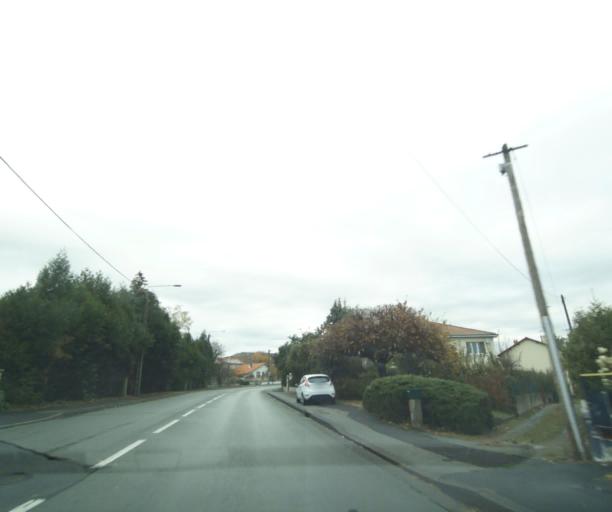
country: FR
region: Auvergne
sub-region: Departement du Puy-de-Dome
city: Cournon-d'Auvergne
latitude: 45.7356
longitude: 3.2053
